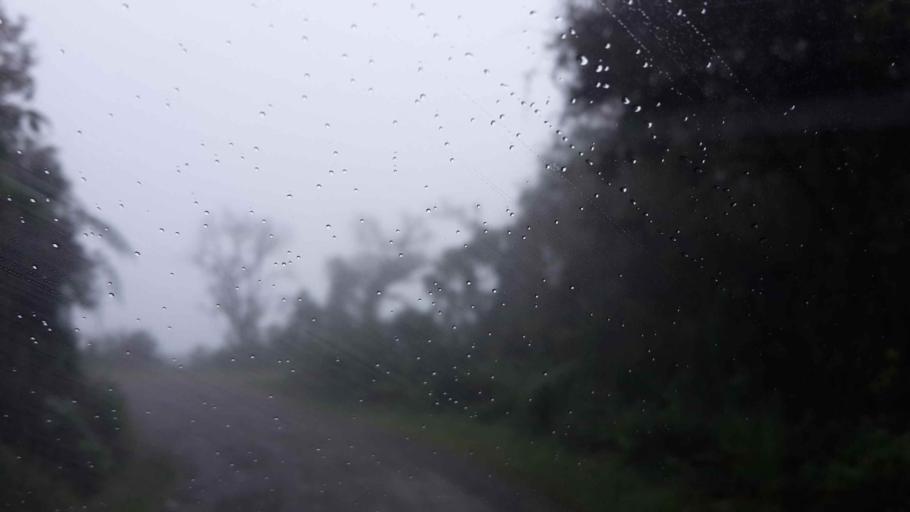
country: BO
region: Cochabamba
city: Colomi
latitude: -17.1086
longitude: -65.9728
